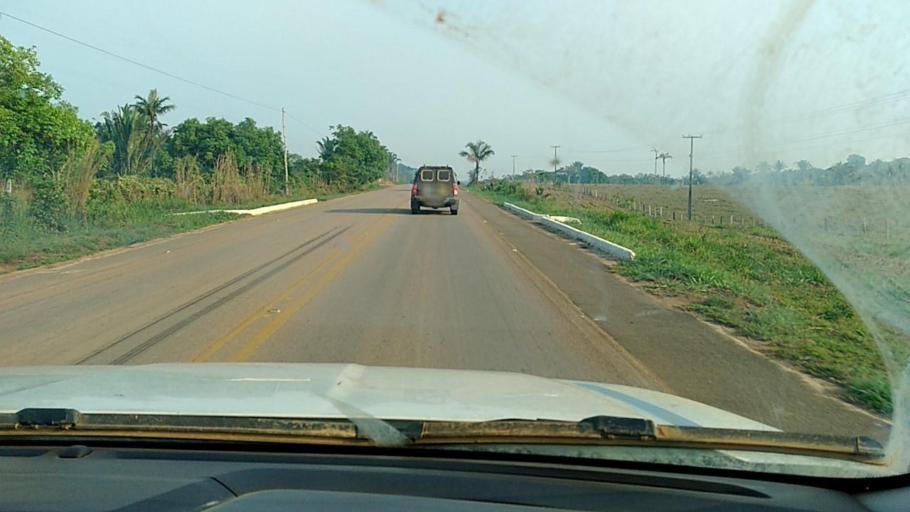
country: BR
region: Rondonia
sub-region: Porto Velho
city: Porto Velho
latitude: -8.7056
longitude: -63.9877
